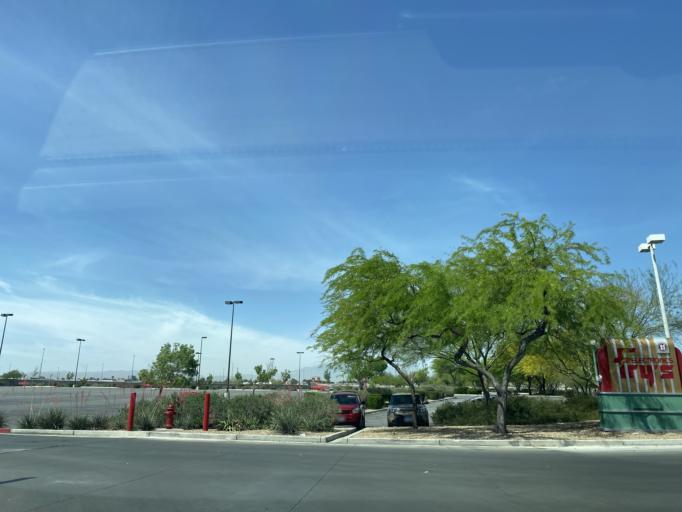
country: US
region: Nevada
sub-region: Clark County
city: Paradise
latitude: 36.0657
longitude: -115.1755
